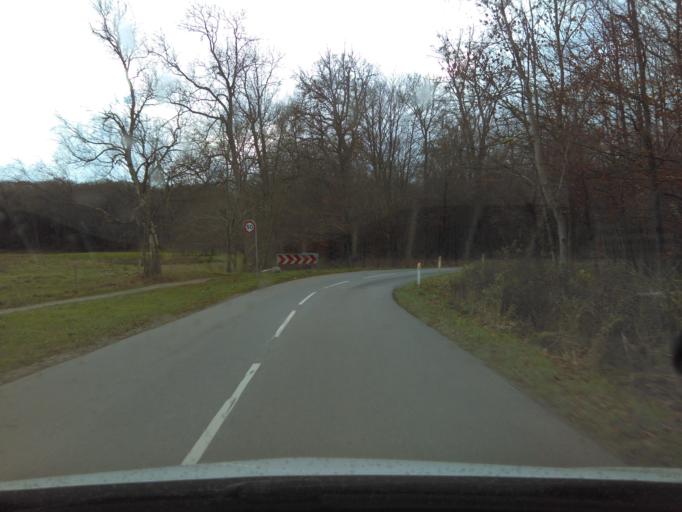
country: DK
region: Capital Region
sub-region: Fureso Kommune
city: Vaerlose
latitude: 55.7621
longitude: 12.3827
